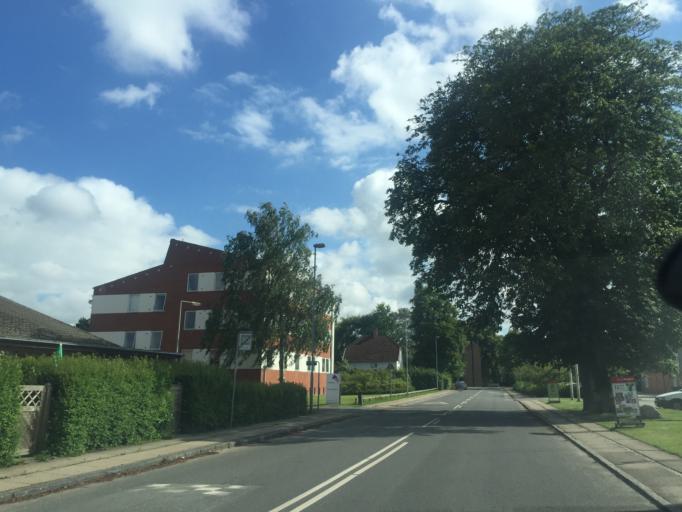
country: DK
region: South Denmark
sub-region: Odense Kommune
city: Odense
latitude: 55.3578
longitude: 10.3897
